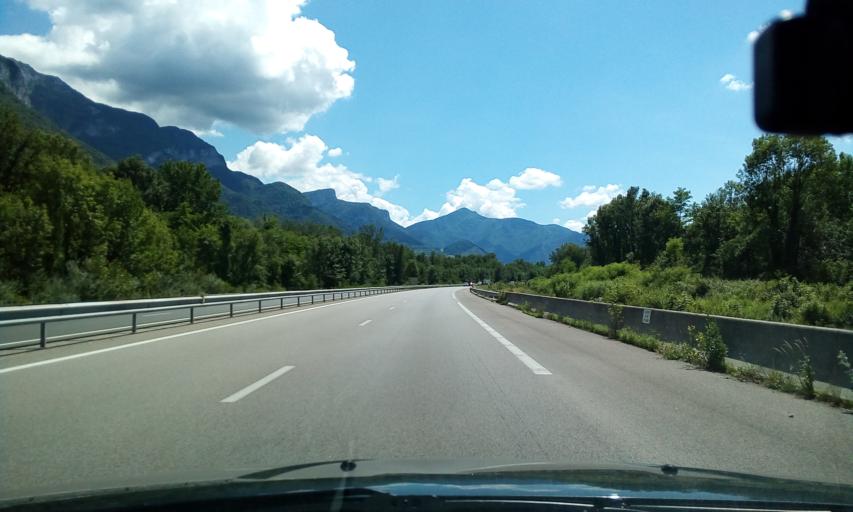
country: FR
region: Rhone-Alpes
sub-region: Departement de l'Isere
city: Saint-Quentin-sur-Isere
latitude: 45.2681
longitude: 5.5193
